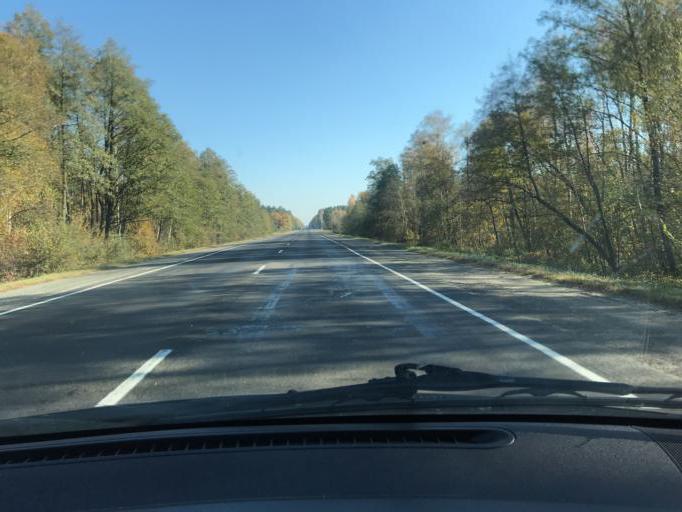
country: BY
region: Brest
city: Mikashevichy
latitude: 52.2415
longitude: 27.4792
